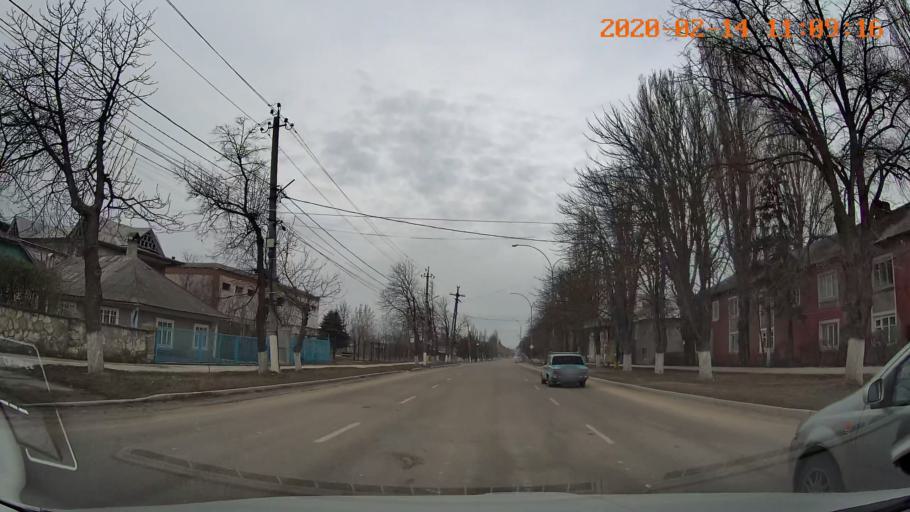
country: MD
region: Raionul Edinet
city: Edinet
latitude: 48.1770
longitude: 27.2954
